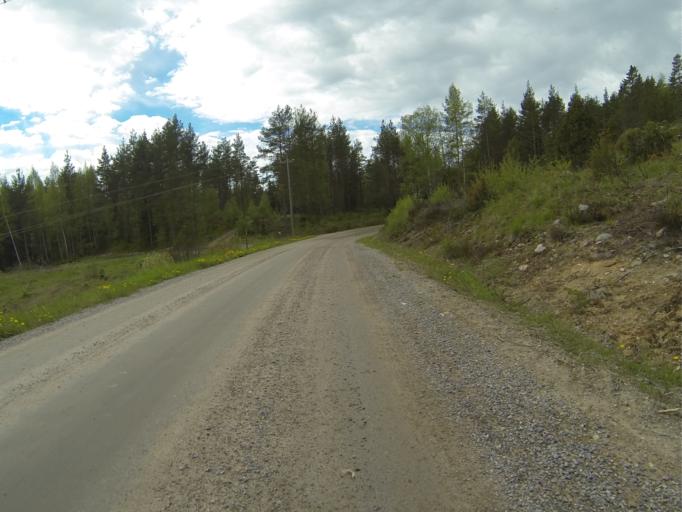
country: FI
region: Varsinais-Suomi
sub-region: Salo
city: Halikko
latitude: 60.3417
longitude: 23.0875
